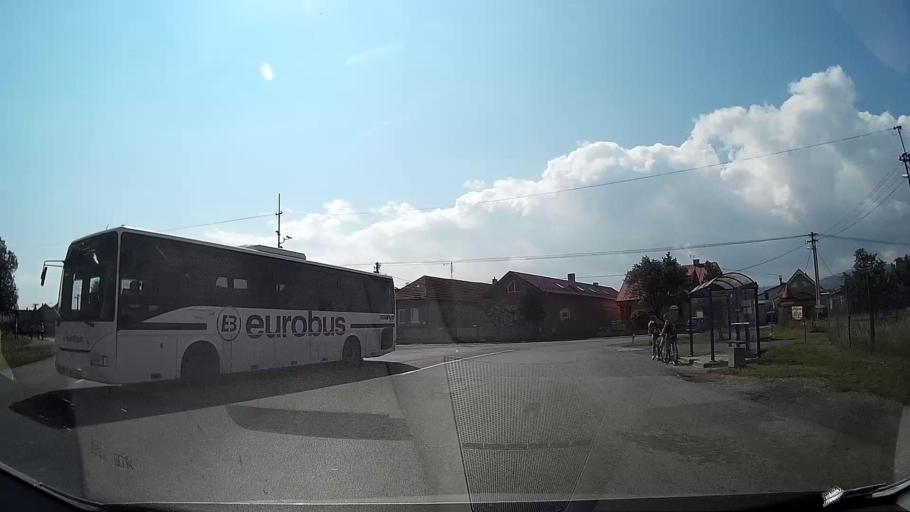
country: SK
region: Kosicky
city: Spisska Nova Ves
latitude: 48.9543
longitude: 20.5122
